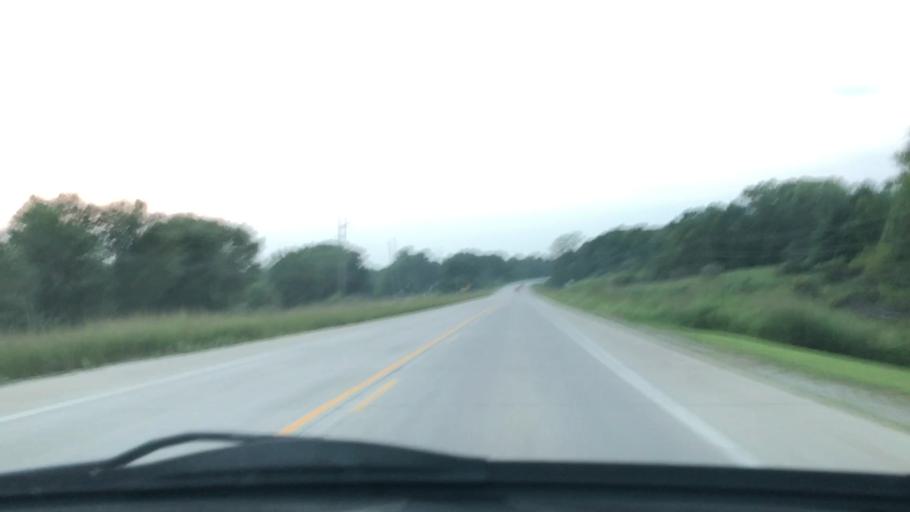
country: US
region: Iowa
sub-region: Johnson County
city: North Liberty
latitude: 41.8124
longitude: -91.6631
